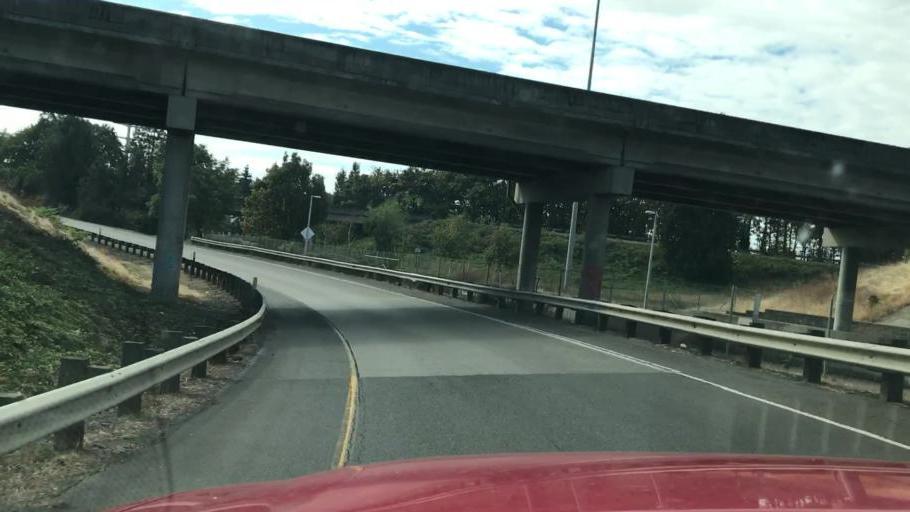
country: US
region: Oregon
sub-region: Lane County
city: Springfield
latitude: 44.0624
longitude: -123.0516
